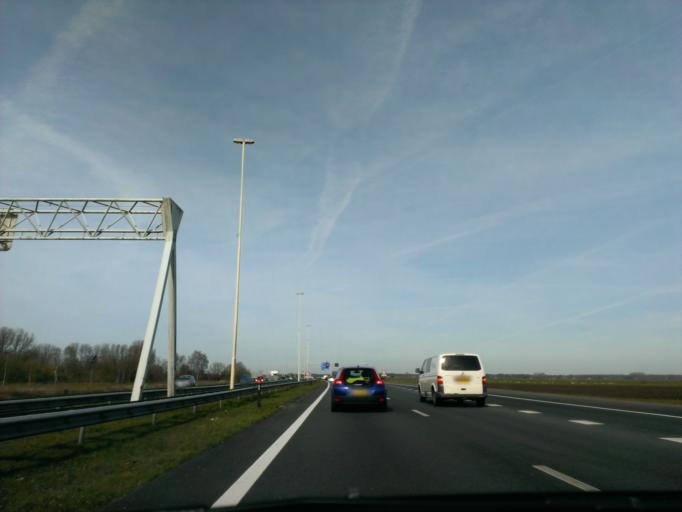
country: NL
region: Utrecht
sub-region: Gemeente Baarn
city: Baarn
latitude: 52.2220
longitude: 5.2925
